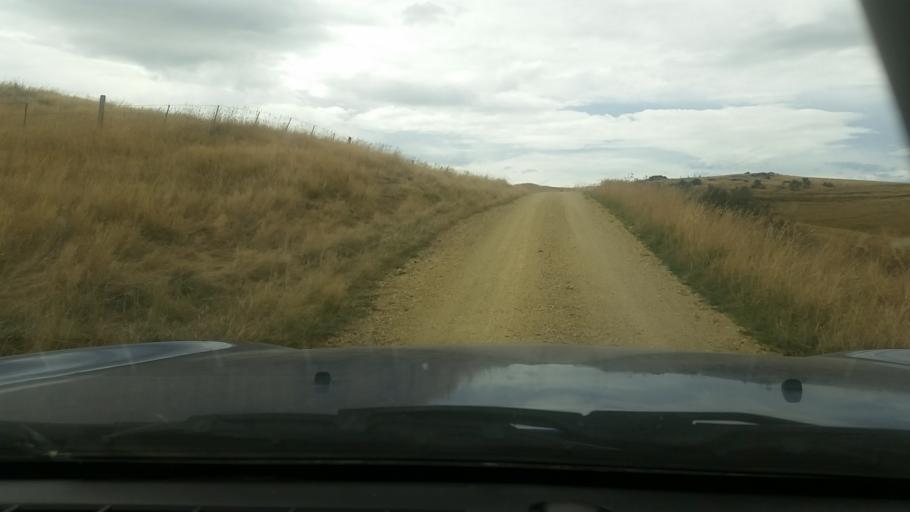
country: NZ
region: Southland
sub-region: Gore District
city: Gore
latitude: -45.5836
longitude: 169.4103
